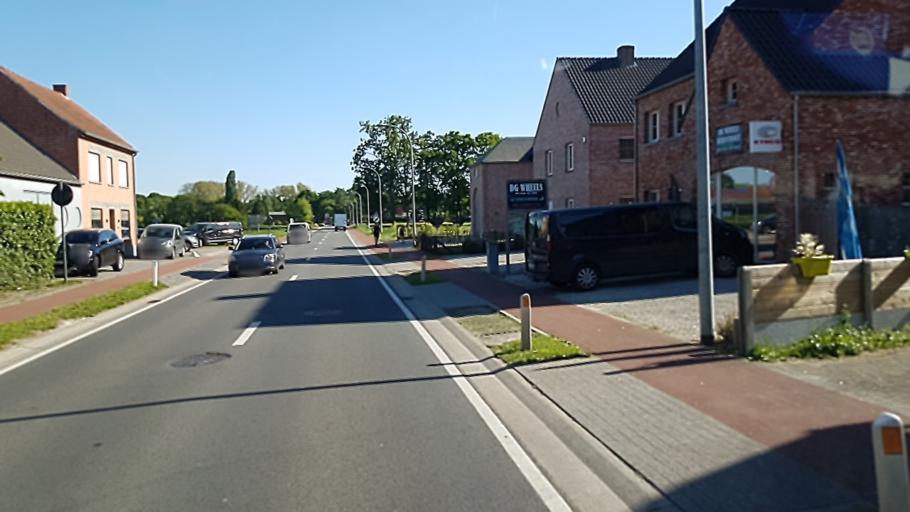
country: BE
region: Flanders
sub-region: Provincie Antwerpen
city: Herenthout
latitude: 51.1281
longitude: 4.7611
